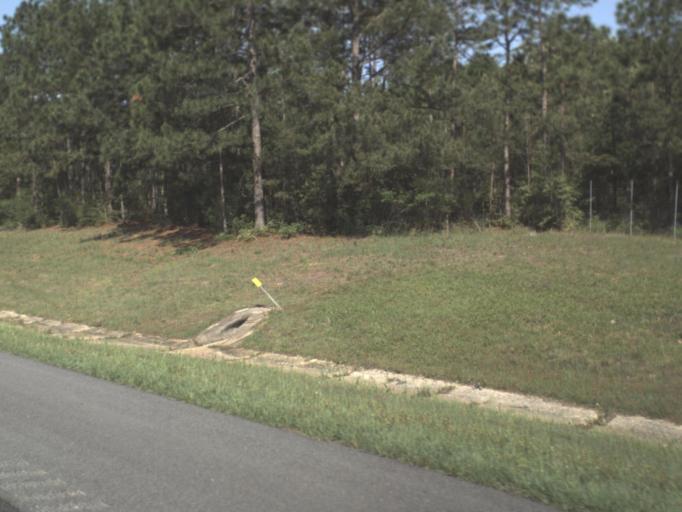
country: US
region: Florida
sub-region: Walton County
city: DeFuniak Springs
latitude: 30.7225
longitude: -85.9150
